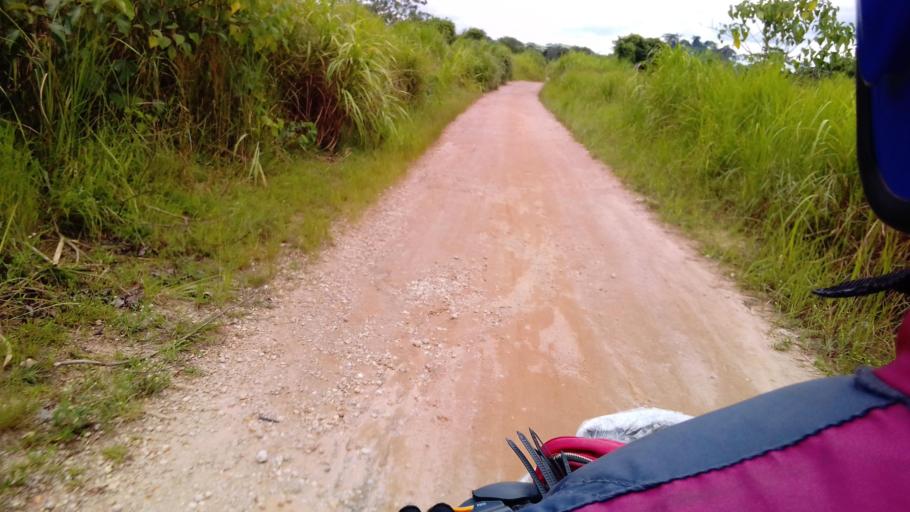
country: SL
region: Eastern Province
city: Koidu
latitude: 8.6807
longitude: -10.9633
